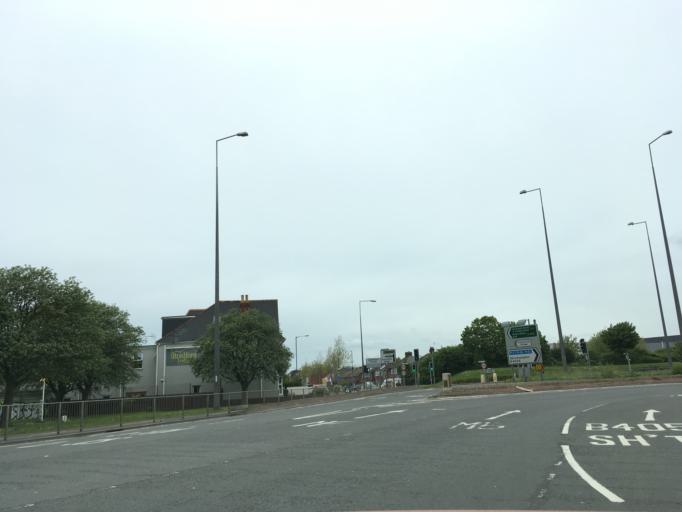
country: GB
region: England
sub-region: North Somerset
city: Easton-in-Gordano
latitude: 51.4977
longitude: -2.6907
